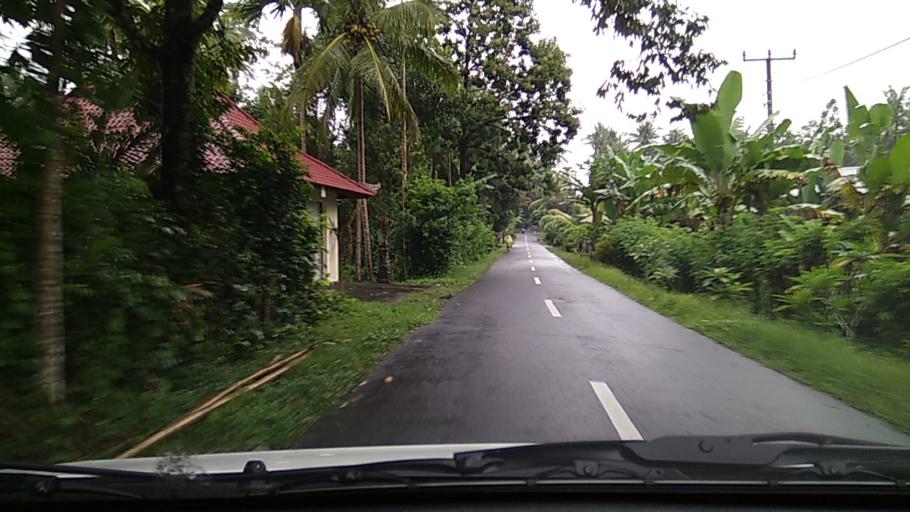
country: ID
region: Bali
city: Tiyingtali Kelod
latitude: -8.3948
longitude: 115.6160
